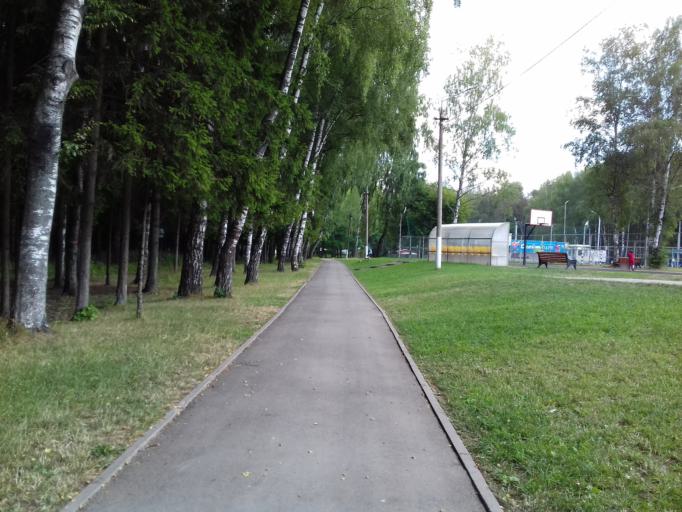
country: RU
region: Tula
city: Tula
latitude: 54.1816
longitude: 37.5840
